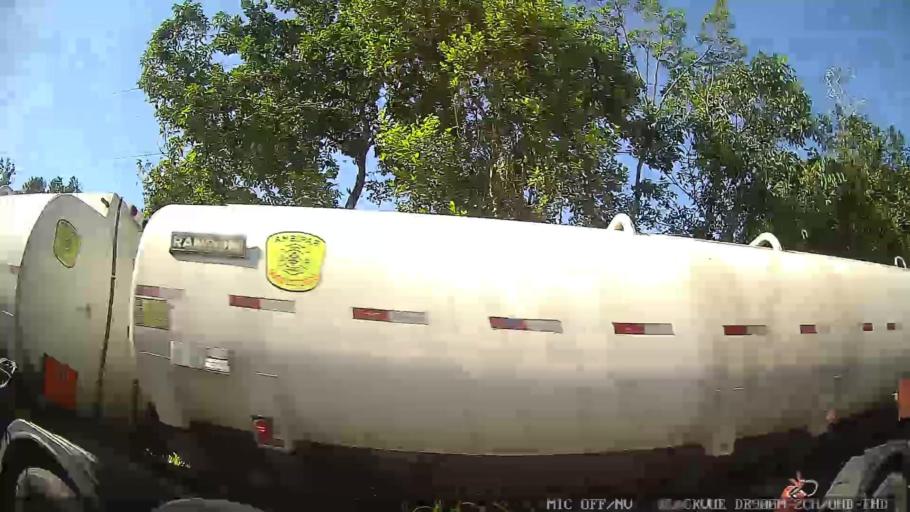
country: BR
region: Sao Paulo
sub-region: Santos
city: Santos
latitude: -23.8998
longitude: -46.3026
